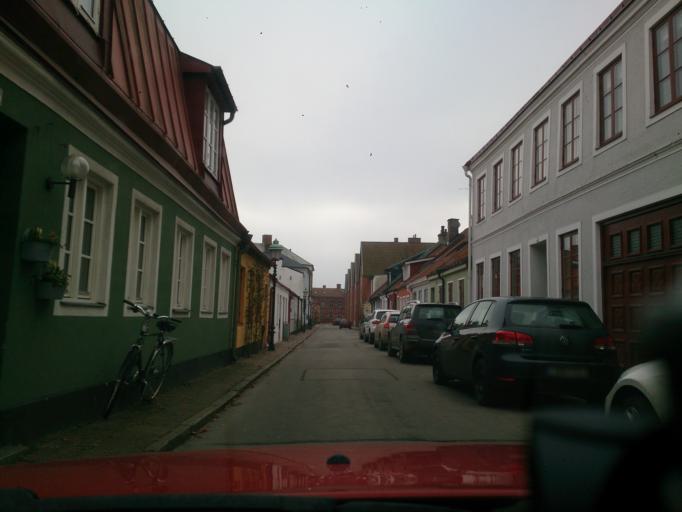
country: SE
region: Skane
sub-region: Ystads Kommun
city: Ystad
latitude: 55.4310
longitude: 13.8156
